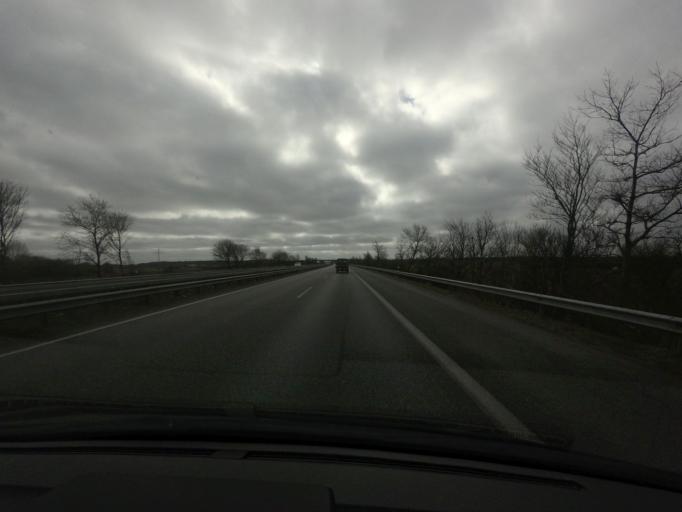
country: DE
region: Schleswig-Holstein
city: Bollingstedt
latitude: 54.6068
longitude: 9.4482
